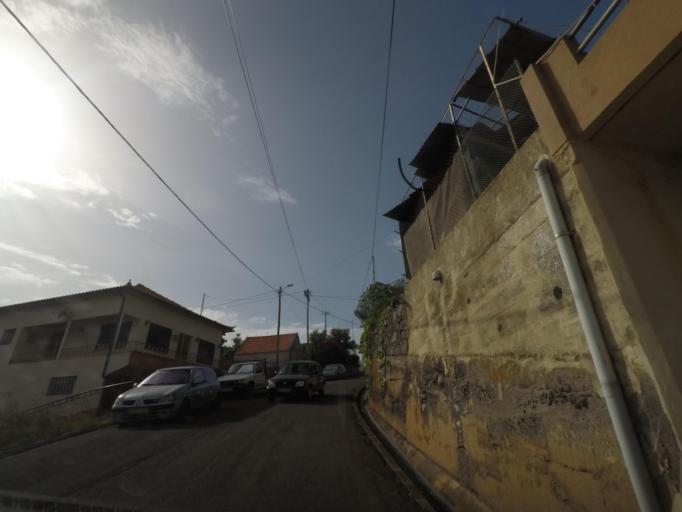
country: PT
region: Madeira
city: Ponta do Sol
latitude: 32.6963
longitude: -17.1179
